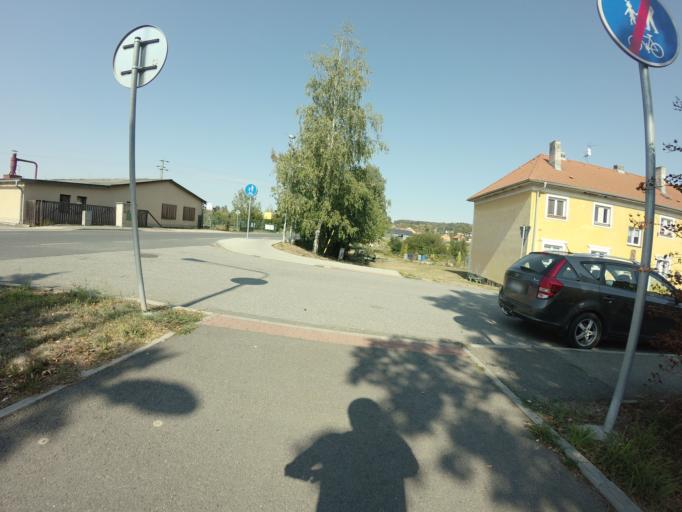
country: CZ
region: Central Bohemia
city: Tynec nad Sazavou
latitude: 49.8373
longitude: 14.5825
